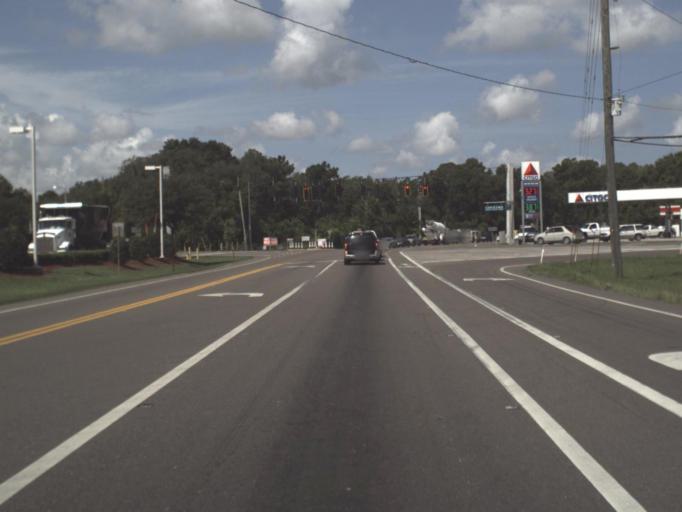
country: US
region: Florida
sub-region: Pasco County
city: Shady Hills
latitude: 28.3216
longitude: -82.5021
